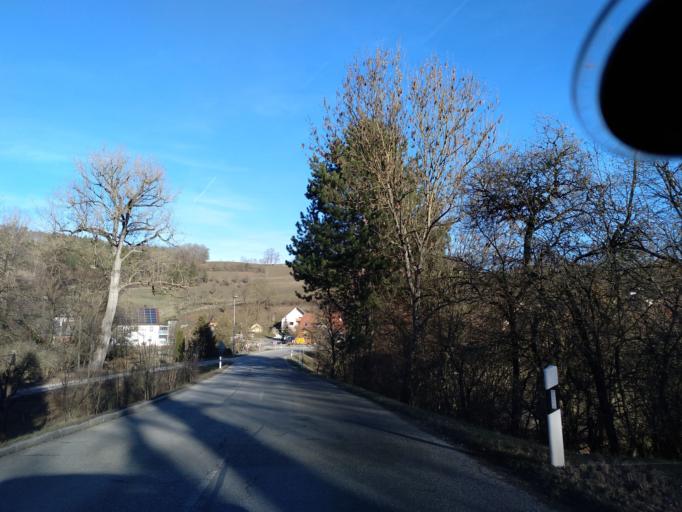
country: DE
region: Baden-Wuerttemberg
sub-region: Regierungsbezirk Stuttgart
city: Vellberg
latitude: 49.0833
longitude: 9.8929
